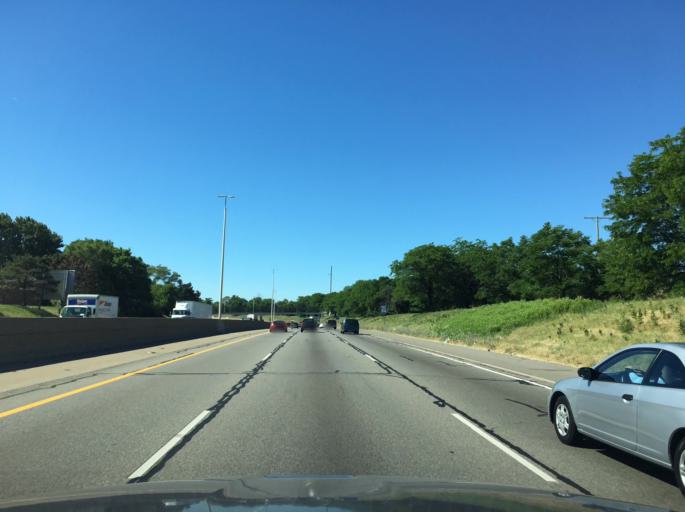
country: US
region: Michigan
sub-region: Wayne County
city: Grosse Pointe Woods
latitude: 42.4610
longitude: -82.9235
